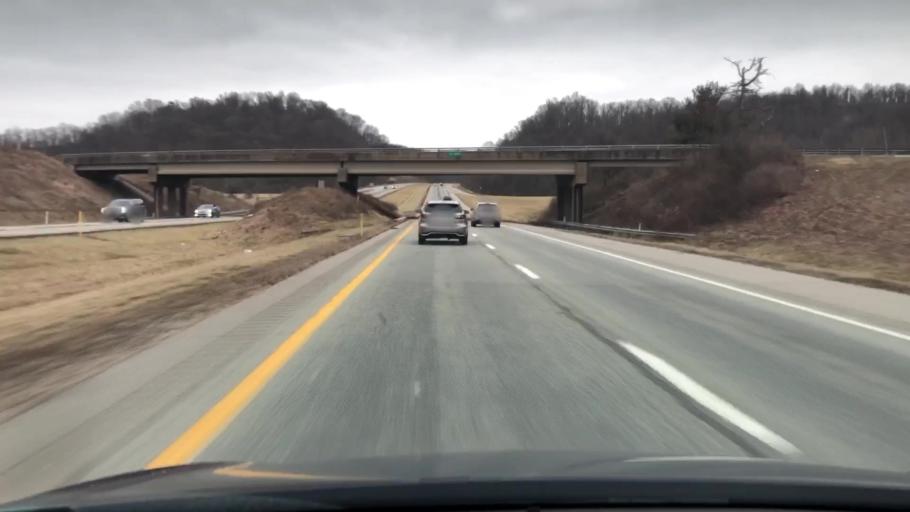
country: US
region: Pennsylvania
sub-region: Greene County
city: Morrisville
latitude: 39.8068
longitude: -80.0910
